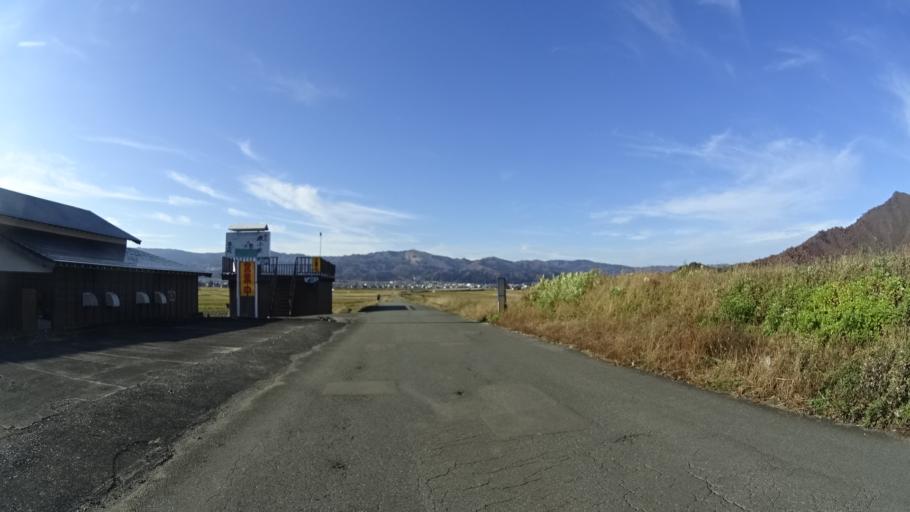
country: JP
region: Niigata
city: Muikamachi
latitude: 37.0358
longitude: 138.8878
